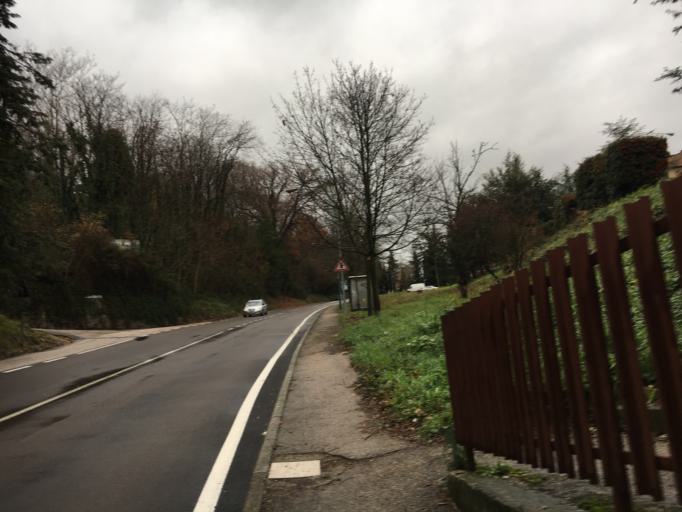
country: IT
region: Umbria
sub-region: Provincia di Perugia
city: Perugia
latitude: 43.1152
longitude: 12.3753
